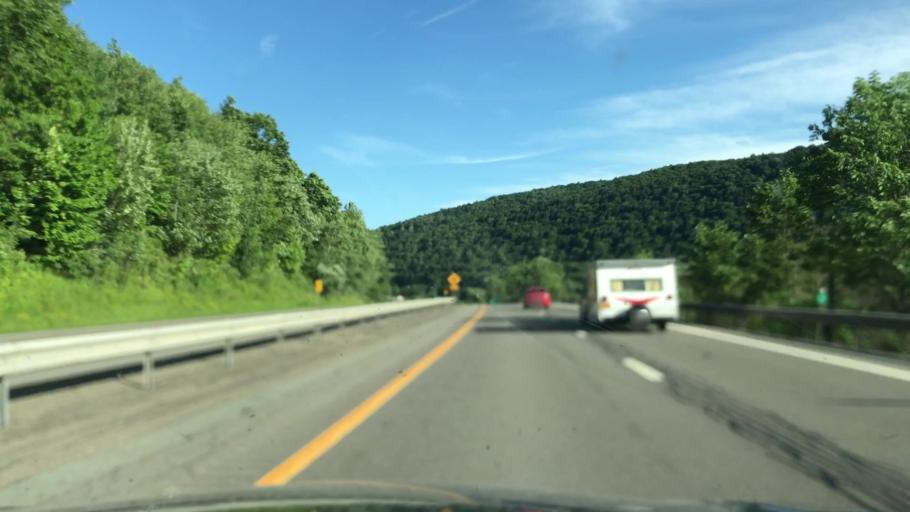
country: US
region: New York
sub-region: Broome County
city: Deposit
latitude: 42.0062
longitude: -75.3618
